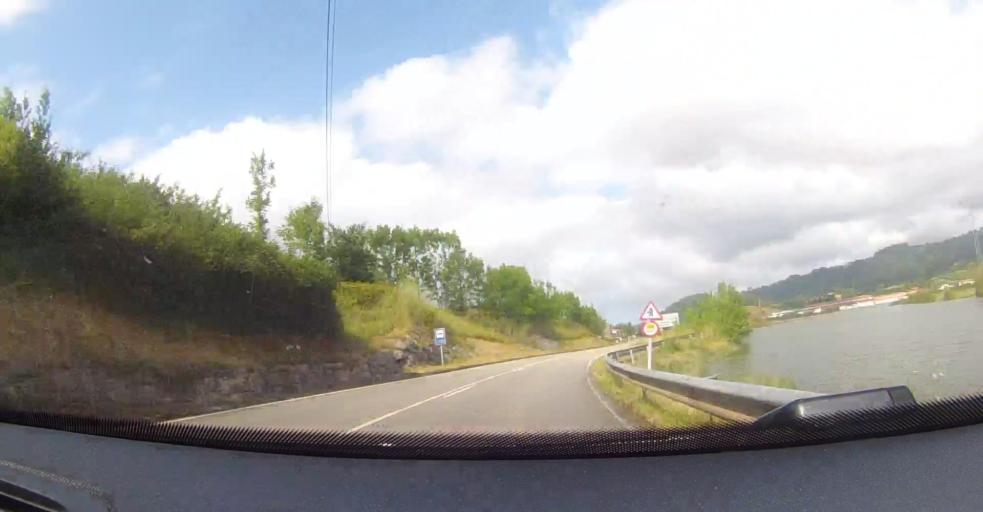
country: ES
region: Asturias
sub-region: Province of Asturias
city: Villaviciosa
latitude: 43.4927
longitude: -5.4338
